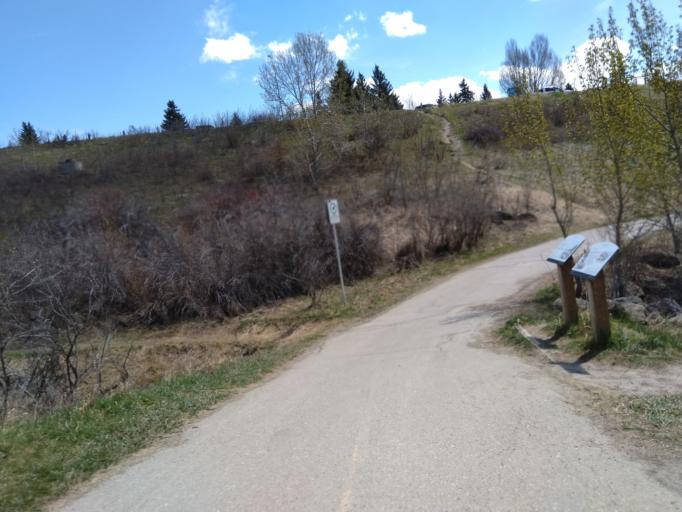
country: CA
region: Alberta
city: Calgary
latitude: 51.1021
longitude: -114.1908
